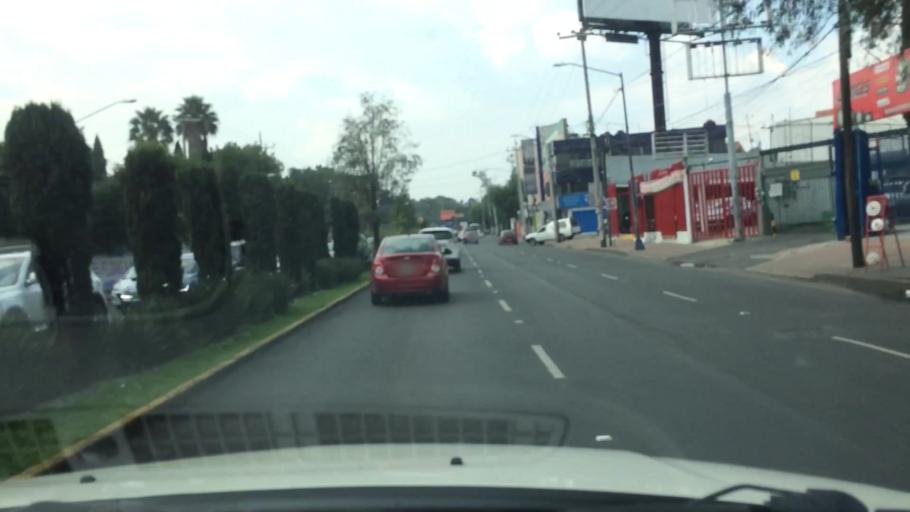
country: MX
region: Mexico City
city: Xochimilco
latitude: 19.2804
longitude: -99.1237
